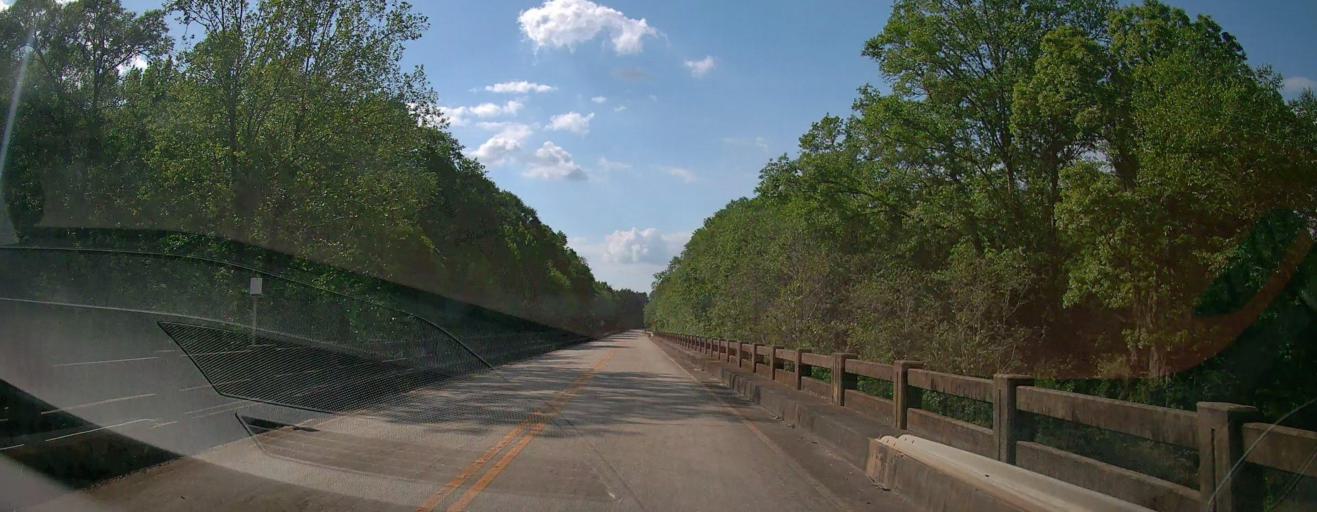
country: US
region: Georgia
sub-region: Washington County
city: Tennille
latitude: 32.8914
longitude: -82.9611
